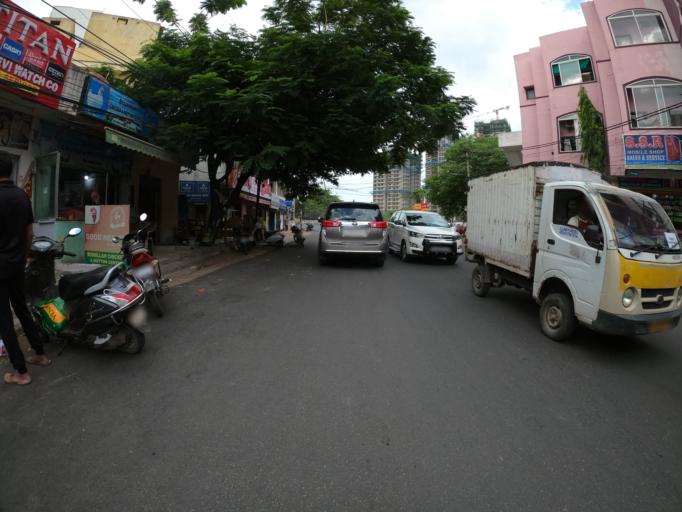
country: IN
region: Telangana
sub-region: Hyderabad
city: Hyderabad
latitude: 17.4087
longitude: 78.3943
